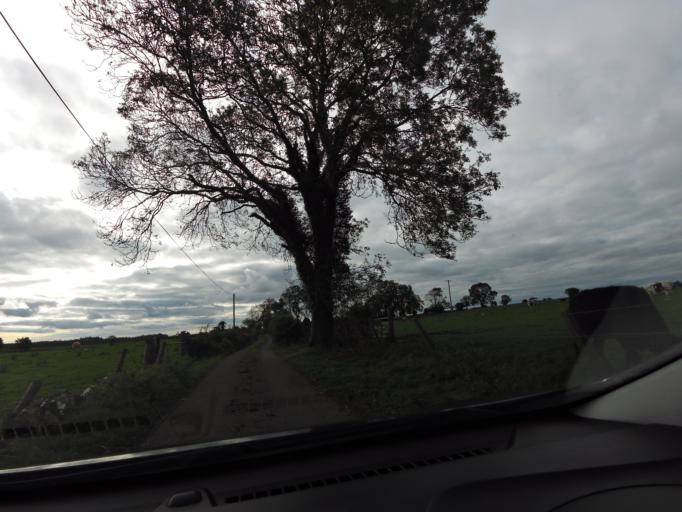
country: IE
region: Connaught
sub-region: County Galway
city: Ballinasloe
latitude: 53.3613
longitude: -8.1078
